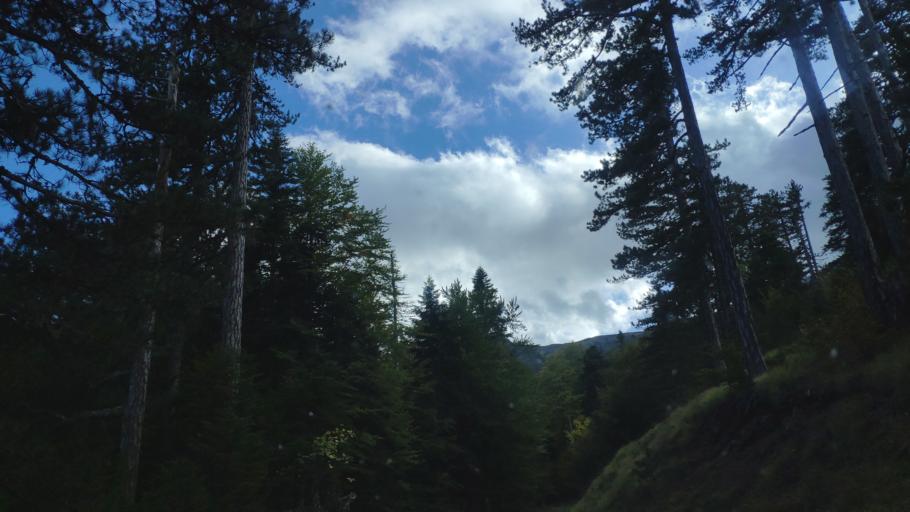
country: AL
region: Korce
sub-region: Rrethi i Devollit
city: Miras
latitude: 40.3366
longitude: 20.9001
